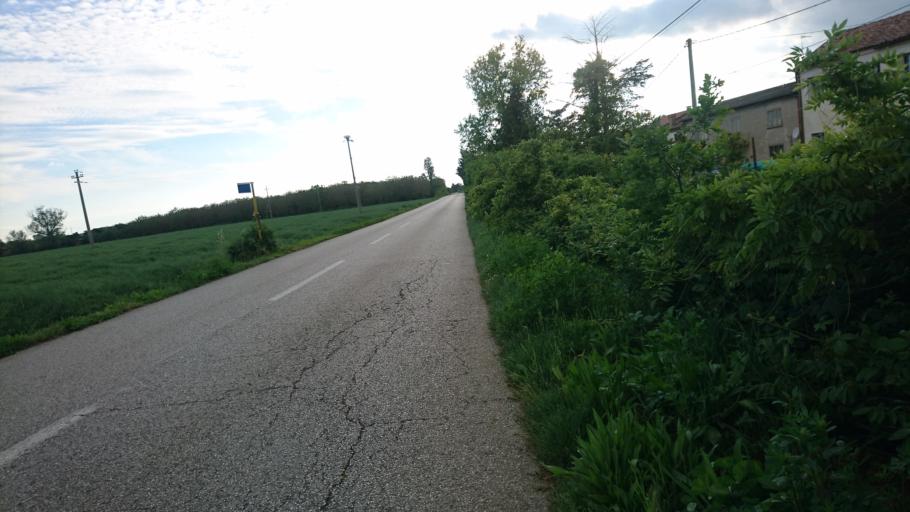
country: IT
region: Veneto
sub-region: Provincia di Rovigo
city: Ceneselli
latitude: 45.0035
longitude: 11.3977
